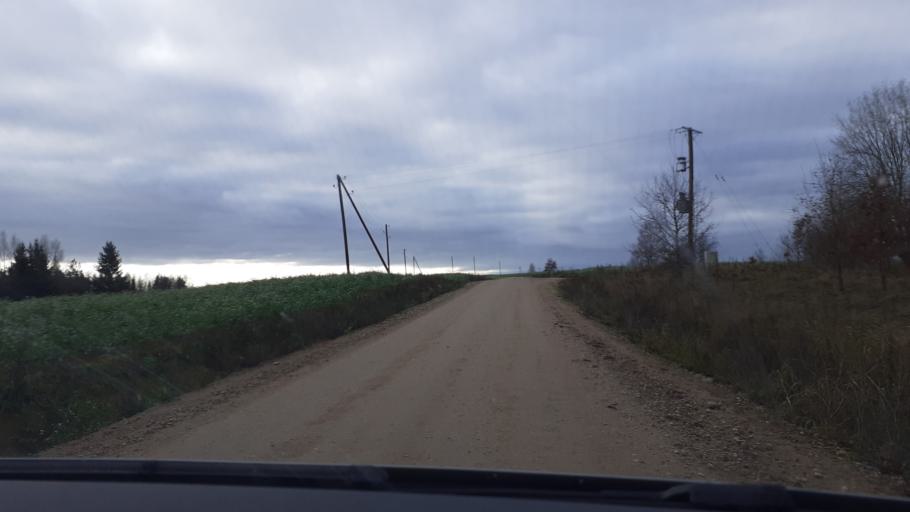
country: LV
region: Aizpute
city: Aizpute
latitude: 56.7724
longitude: 21.8102
